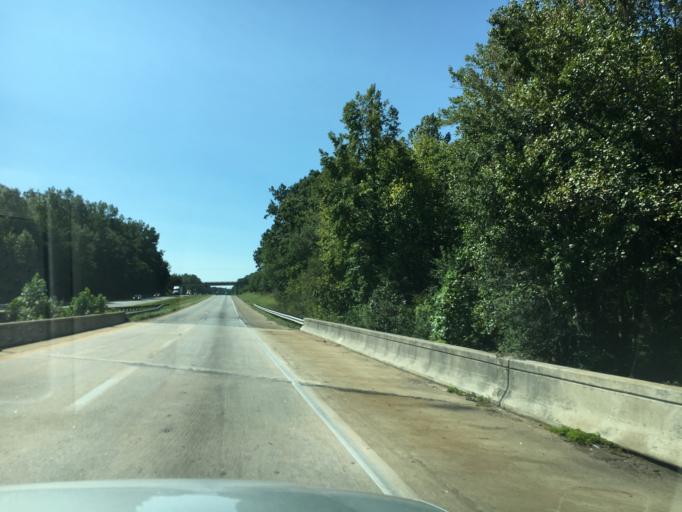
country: US
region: South Carolina
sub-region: Spartanburg County
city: Roebuck
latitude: 34.7903
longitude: -81.9561
